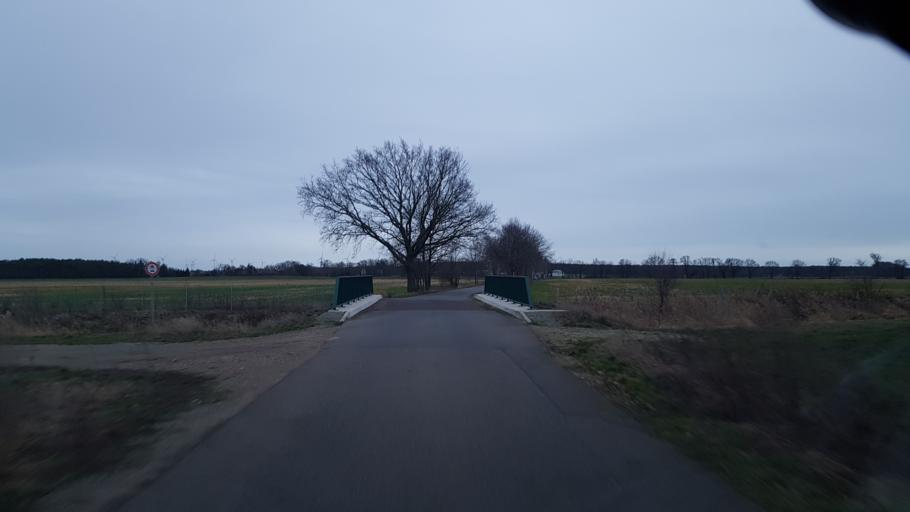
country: DE
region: Brandenburg
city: Schlieben
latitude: 51.7030
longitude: 13.3208
